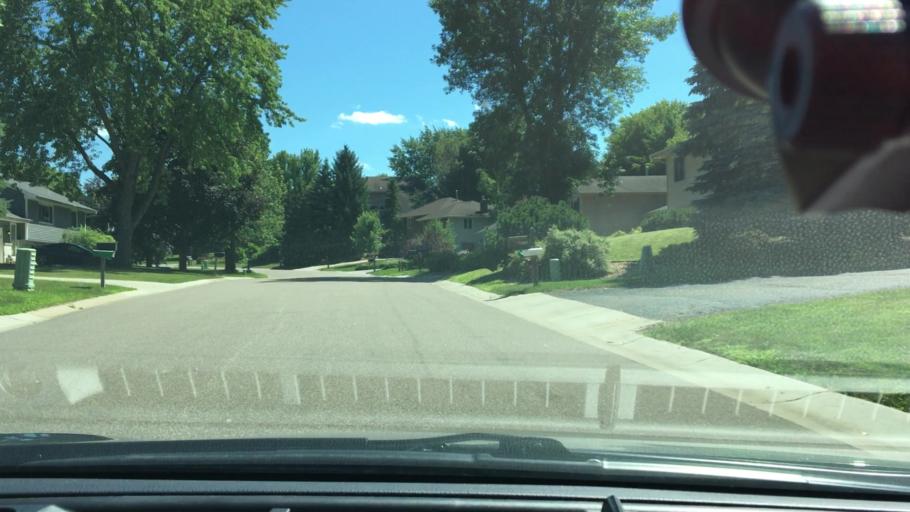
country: US
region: Minnesota
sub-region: Hennepin County
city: Maple Grove
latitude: 45.0692
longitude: -93.4584
